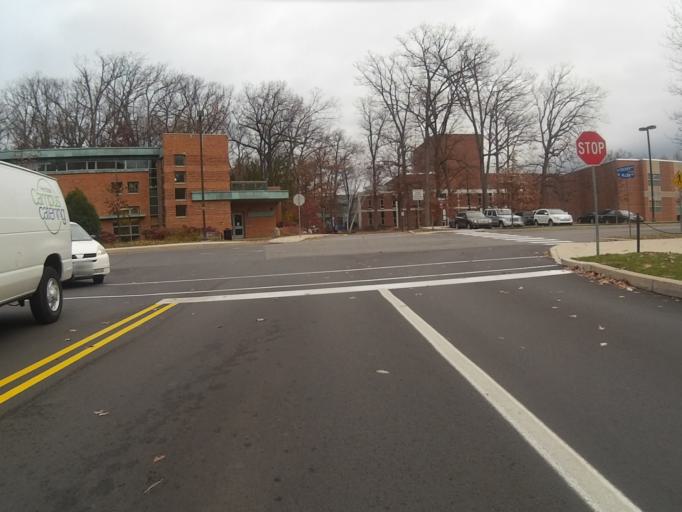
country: US
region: Pennsylvania
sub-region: Centre County
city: State College
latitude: 40.7996
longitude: -77.8687
